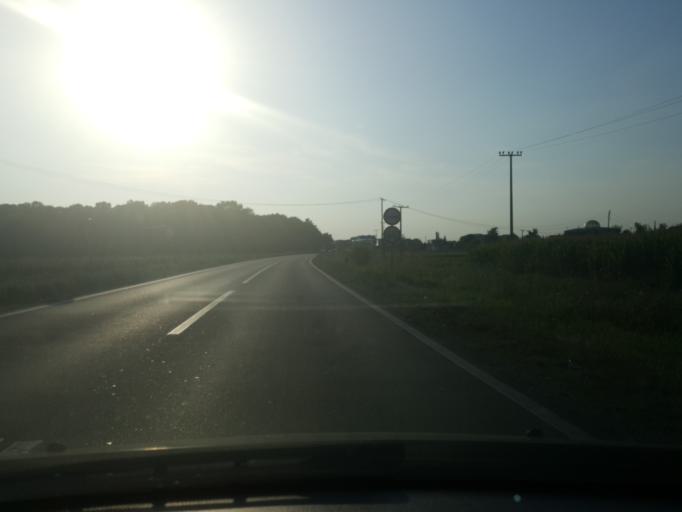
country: RS
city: Majur
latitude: 44.7562
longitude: 19.6523
